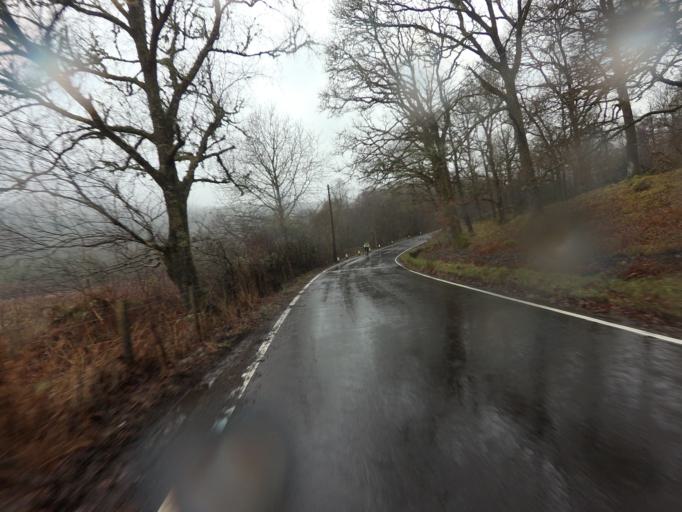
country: GB
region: Scotland
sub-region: Stirling
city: Killearn
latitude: 56.1914
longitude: -4.5085
